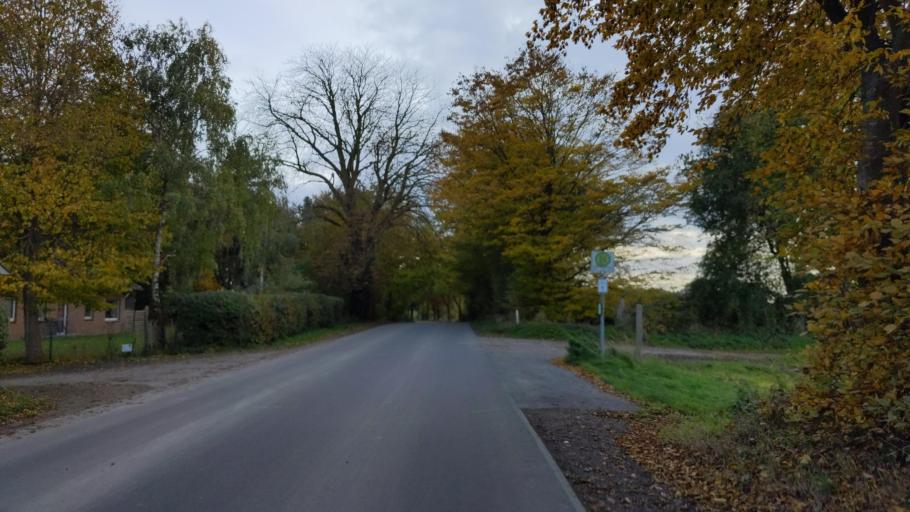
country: DE
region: Schleswig-Holstein
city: Sierksdorf
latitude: 54.0791
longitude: 10.7436
